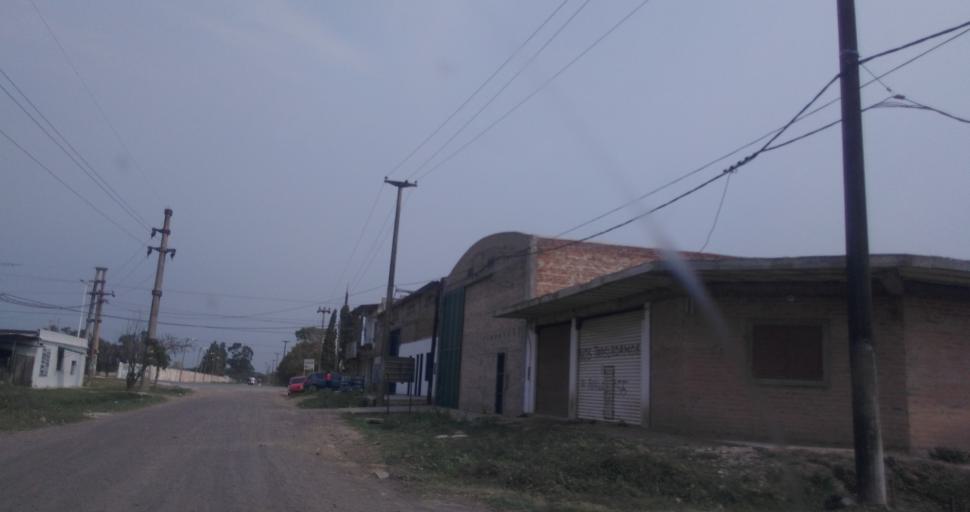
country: AR
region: Chaco
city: Fontana
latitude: -27.4305
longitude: -59.0228
